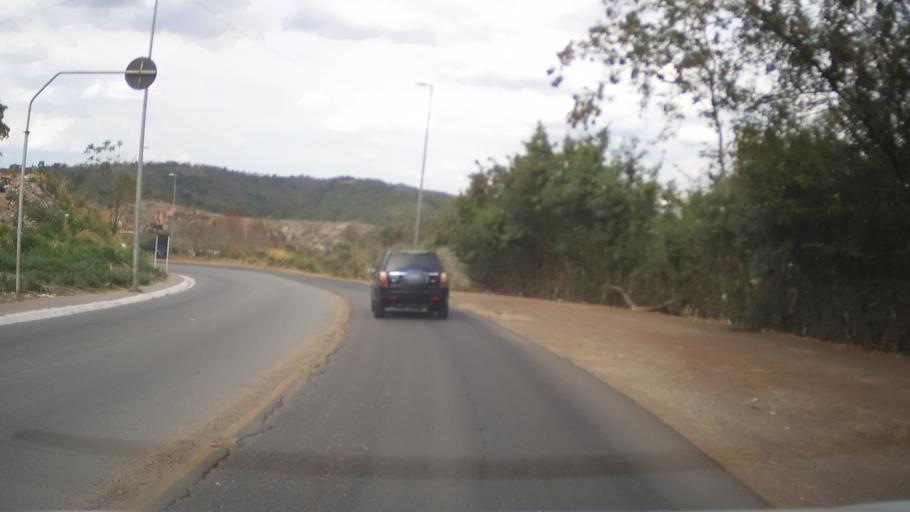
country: BR
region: Minas Gerais
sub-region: Belo Horizonte
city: Belo Horizonte
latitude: -19.8751
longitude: -43.8944
